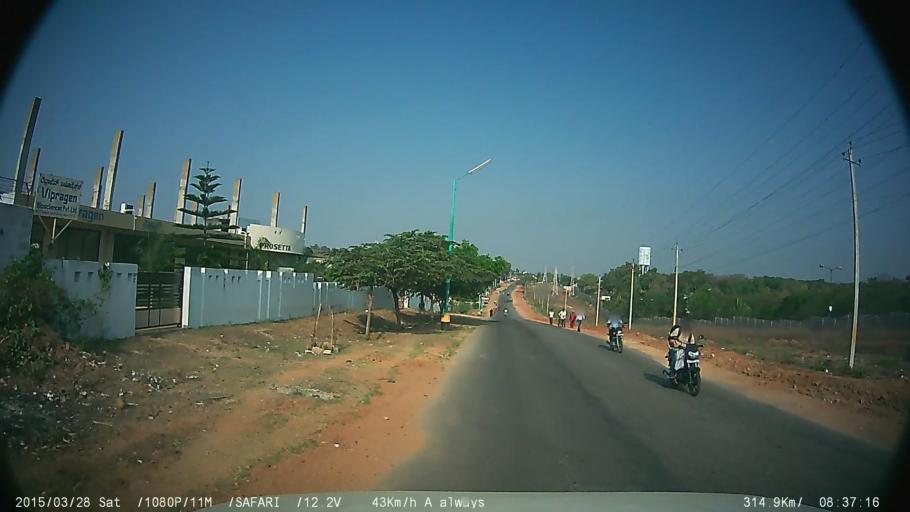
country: IN
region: Karnataka
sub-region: Mysore
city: Mysore
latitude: 12.3567
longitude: 76.5853
